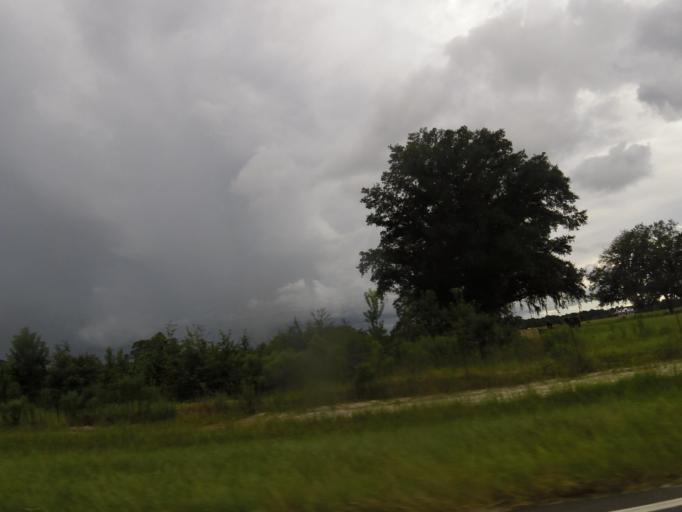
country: US
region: Florida
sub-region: Baker County
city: Macclenny
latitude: 30.4343
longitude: -82.1982
